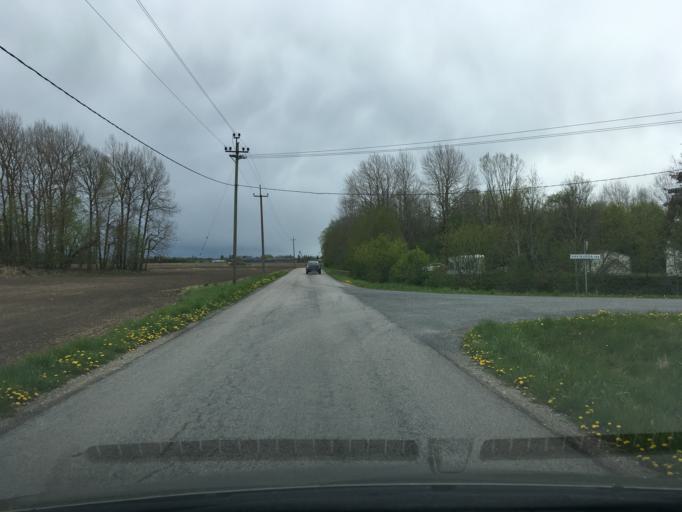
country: EE
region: Harju
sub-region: Joelaehtme vald
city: Loo
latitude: 59.3770
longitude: 24.9661
